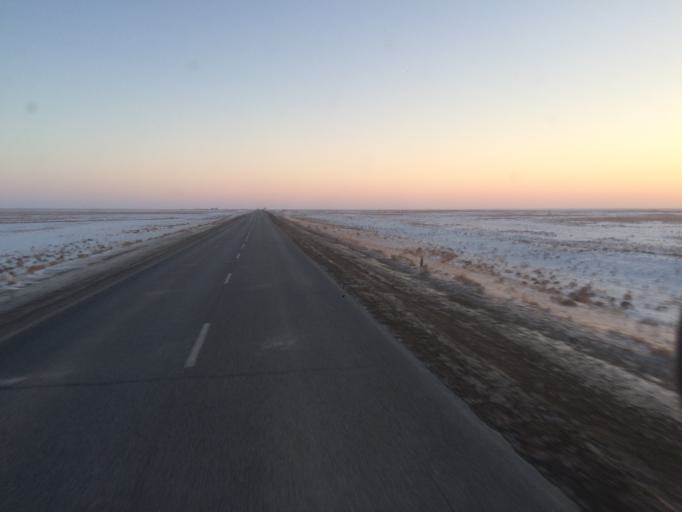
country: KZ
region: Qyzylorda
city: Sekseuil
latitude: 47.4988
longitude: 61.5345
